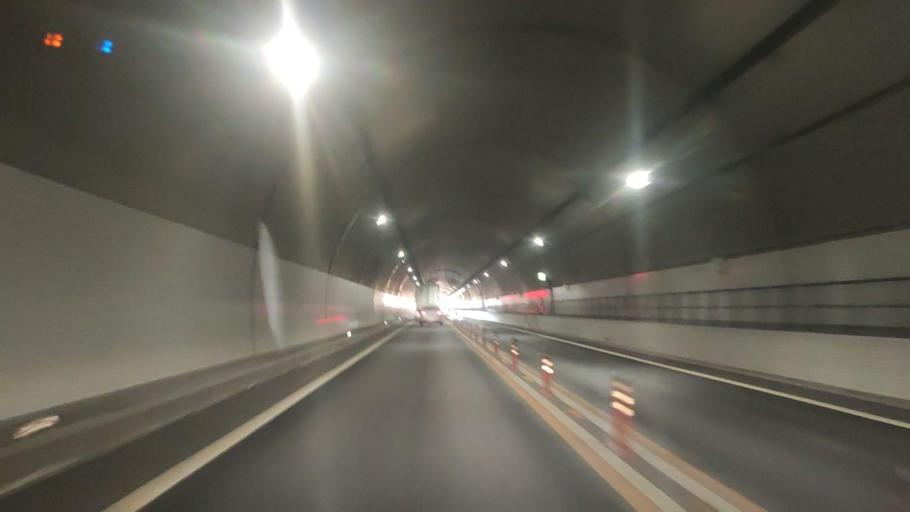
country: JP
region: Fukuoka
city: Kanda
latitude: 33.7665
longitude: 130.9644
